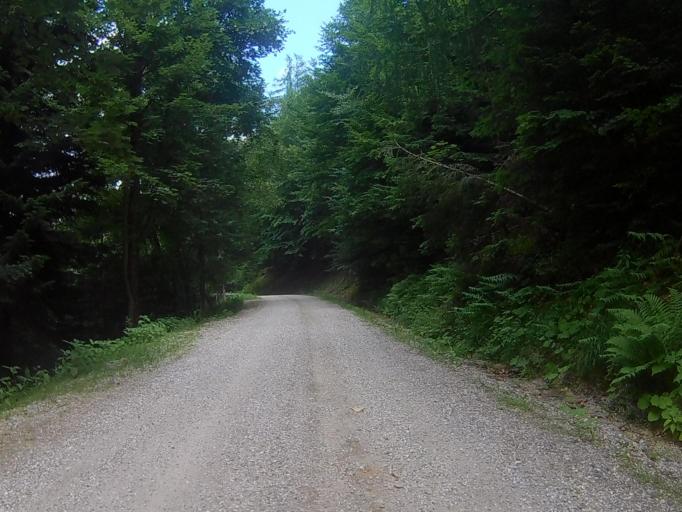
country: SI
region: Ruse
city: Ruse
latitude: 46.5104
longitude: 15.5052
